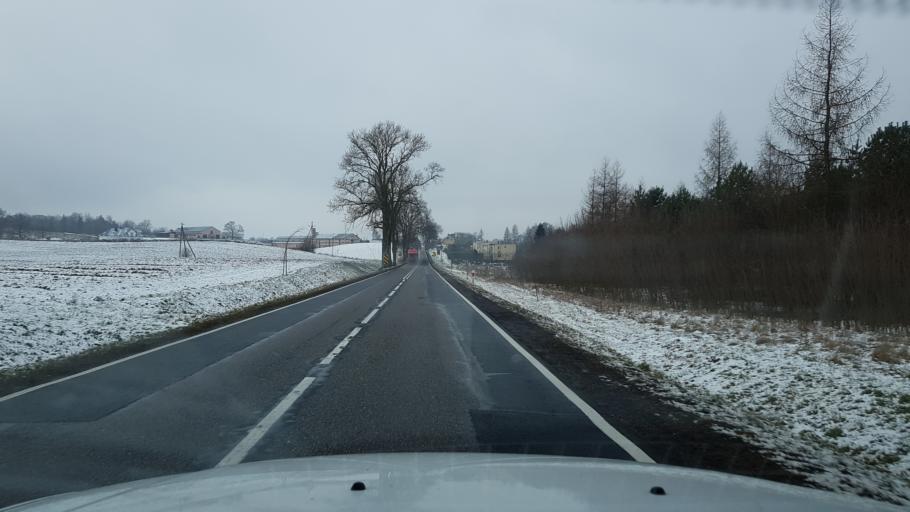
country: PL
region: West Pomeranian Voivodeship
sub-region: Powiat drawski
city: Czaplinek
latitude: 53.5600
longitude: 16.1447
